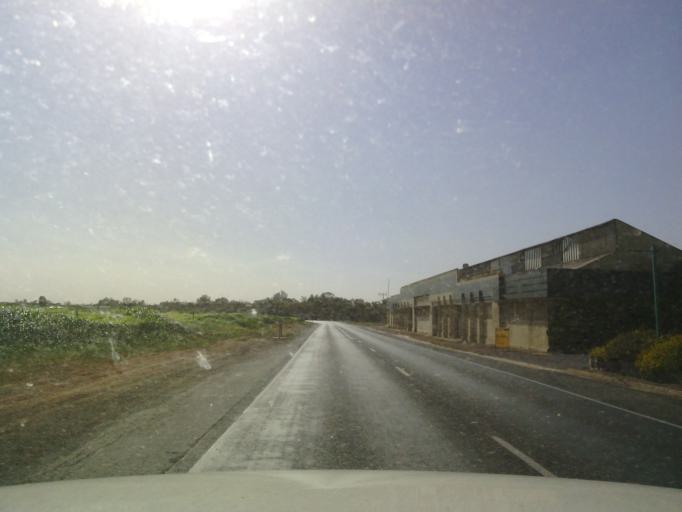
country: AU
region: South Australia
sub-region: Berri and Barmera
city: Berri
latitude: -34.2807
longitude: 140.5729
